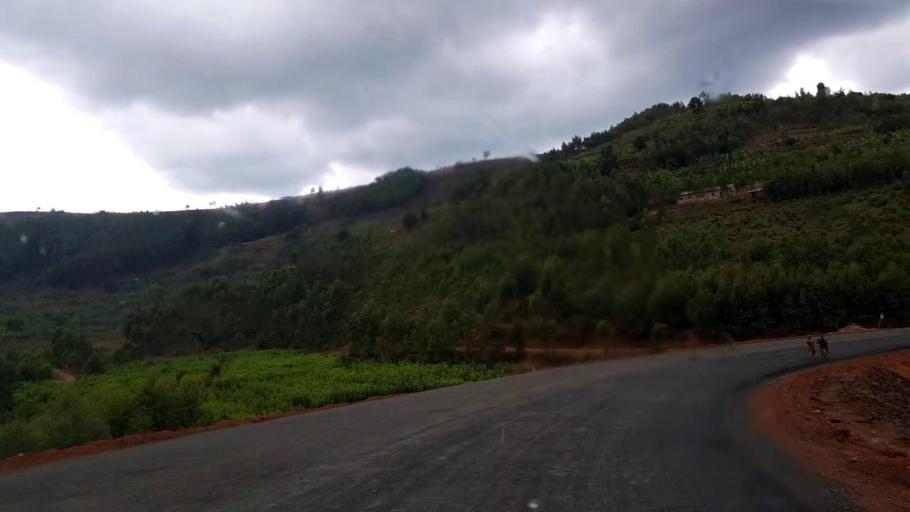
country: RW
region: Northern Province
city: Byumba
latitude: -1.6094
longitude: 30.2358
